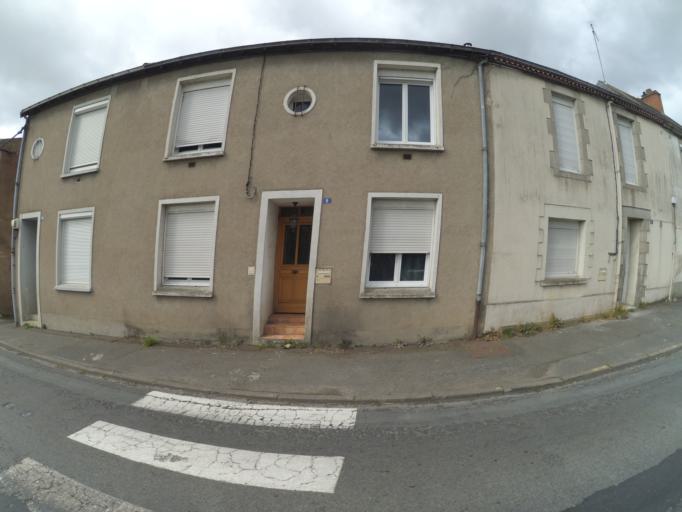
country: FR
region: Pays de la Loire
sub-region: Departement de Maine-et-Loire
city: Montfaucon-Montigne
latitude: 47.0980
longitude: -1.1265
